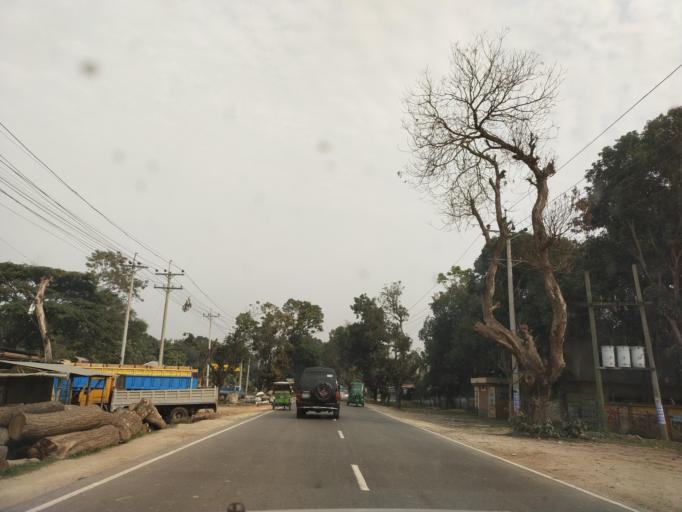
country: BD
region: Dhaka
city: Narsingdi
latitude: 23.9827
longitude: 90.7344
